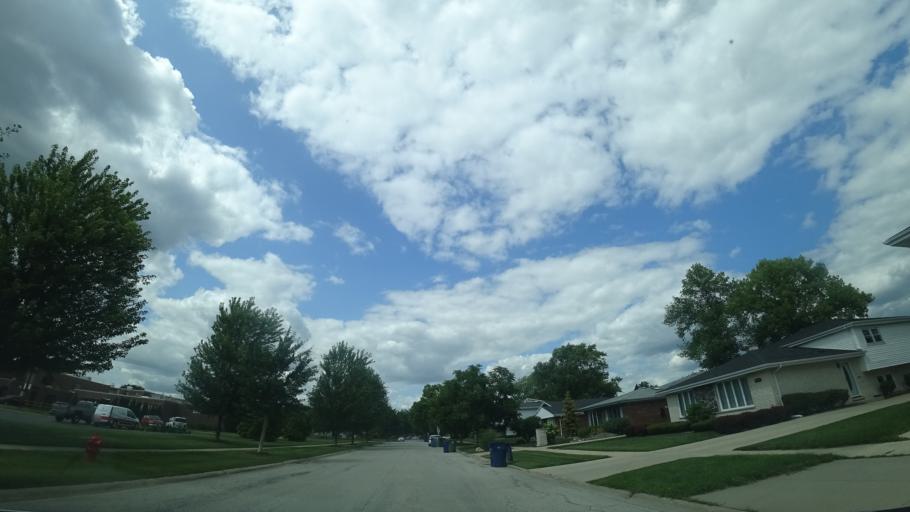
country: US
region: Illinois
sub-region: Cook County
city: Oak Lawn
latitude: 41.6965
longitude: -87.7351
